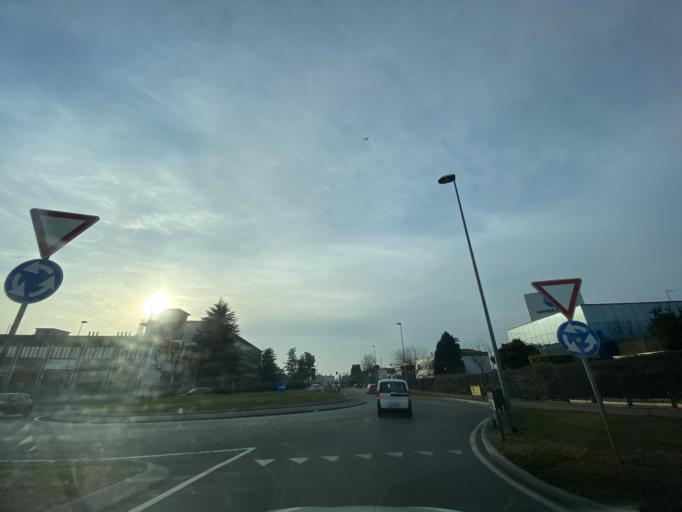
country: IT
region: Lombardy
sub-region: Citta metropolitana di Milano
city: Vimodrone
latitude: 45.5136
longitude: 9.3008
